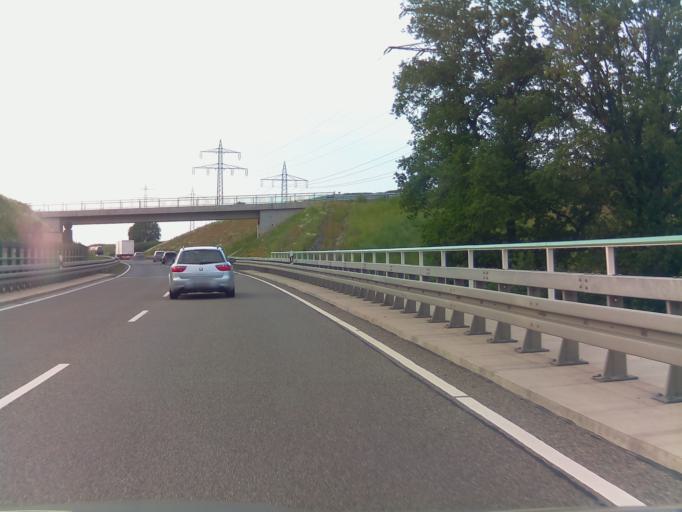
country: DE
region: Hesse
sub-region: Regierungsbezirk Kassel
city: Bad Hersfeld
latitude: 50.8357
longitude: 9.7292
